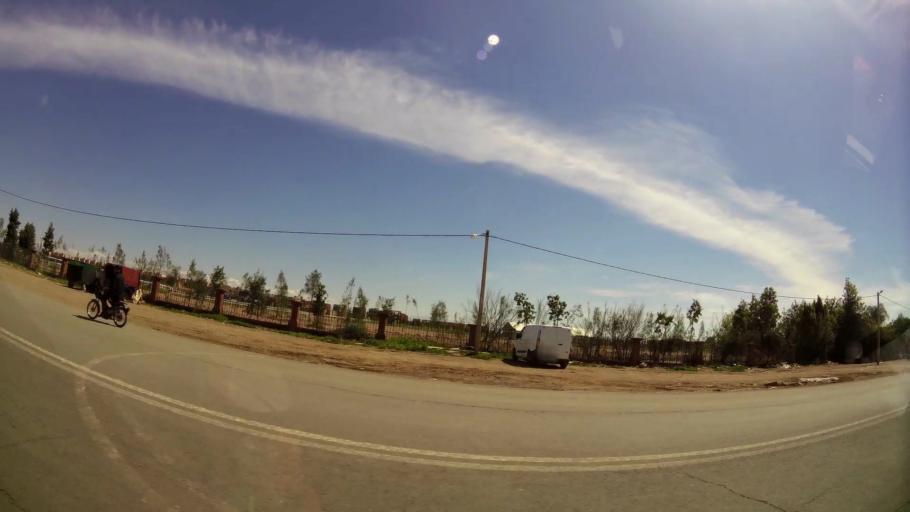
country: MA
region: Marrakech-Tensift-Al Haouz
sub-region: Marrakech
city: Marrakesh
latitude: 31.6405
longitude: -8.1009
